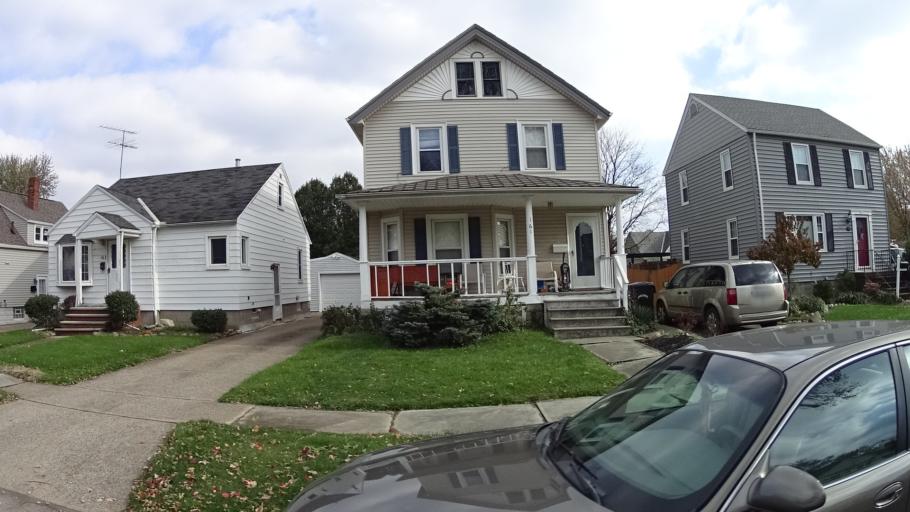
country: US
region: Ohio
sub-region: Lorain County
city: Elyria
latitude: 41.3768
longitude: -82.0871
